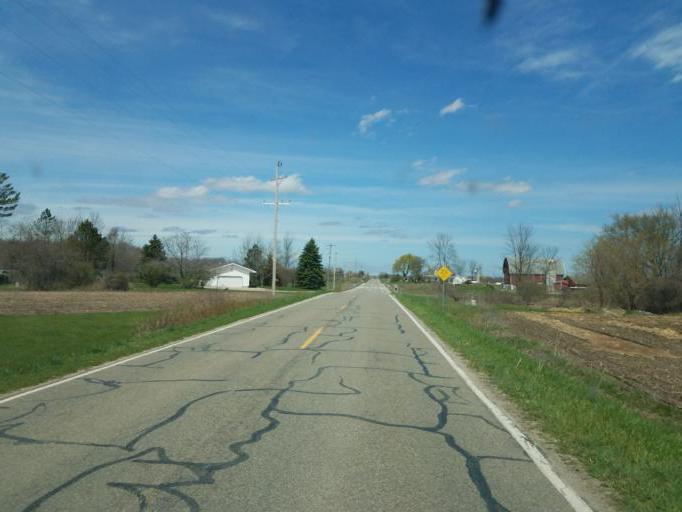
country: US
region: Michigan
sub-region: Isabella County
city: Mount Pleasant
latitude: 43.6727
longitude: -84.7080
